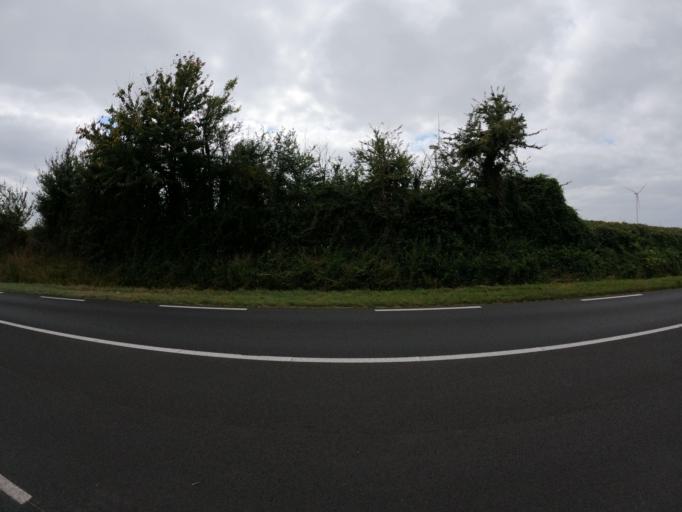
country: FR
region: Poitou-Charentes
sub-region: Departement des Deux-Sevres
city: Melle
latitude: 46.2357
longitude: -0.1711
